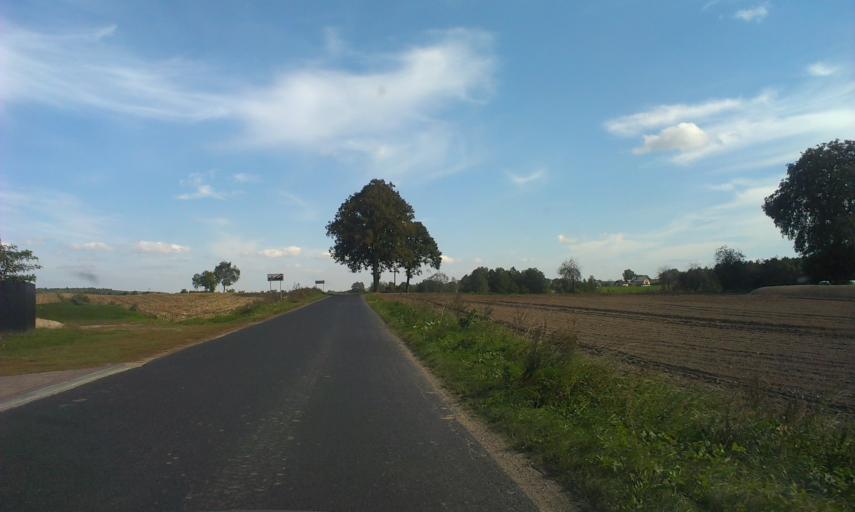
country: PL
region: Greater Poland Voivodeship
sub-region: Powiat pilski
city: Lobzenica
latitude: 53.2779
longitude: 17.2059
